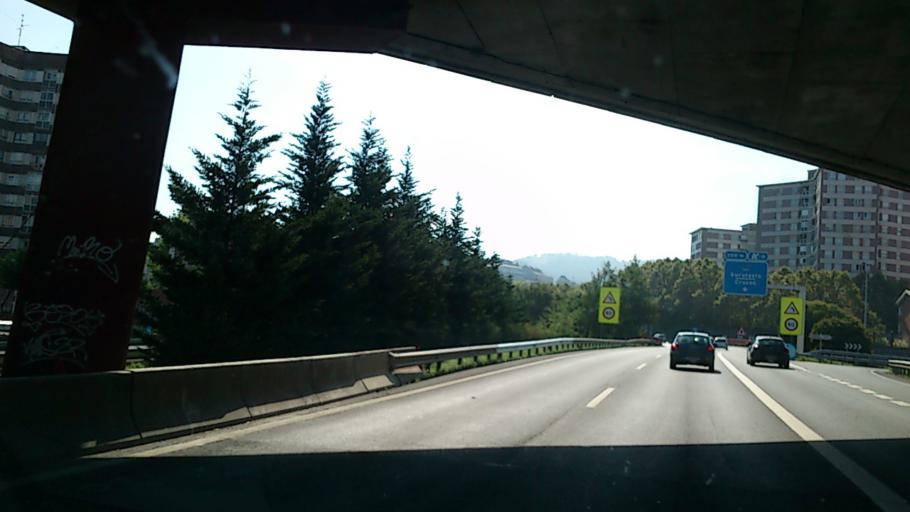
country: ES
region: Basque Country
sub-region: Bizkaia
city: Barakaldo
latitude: 43.2855
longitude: -2.9867
